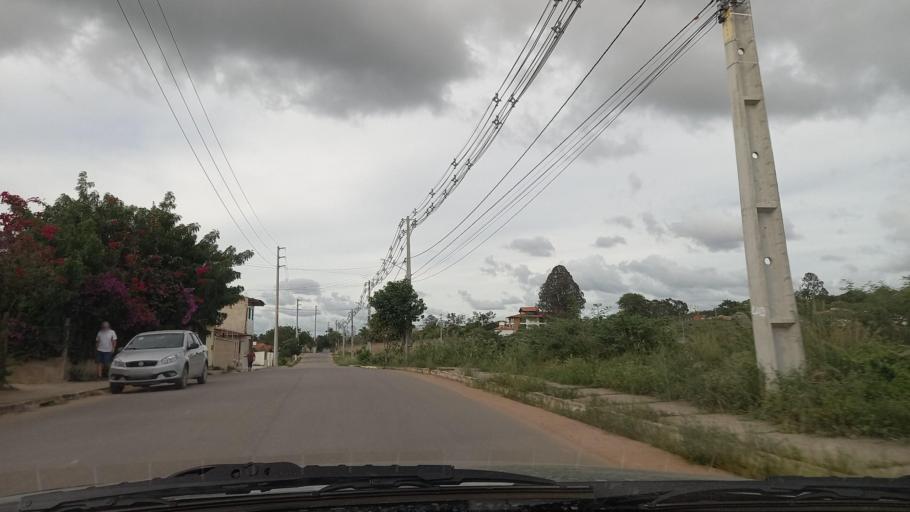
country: BR
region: Pernambuco
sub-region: Gravata
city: Gravata
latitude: -8.2023
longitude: -35.5479
